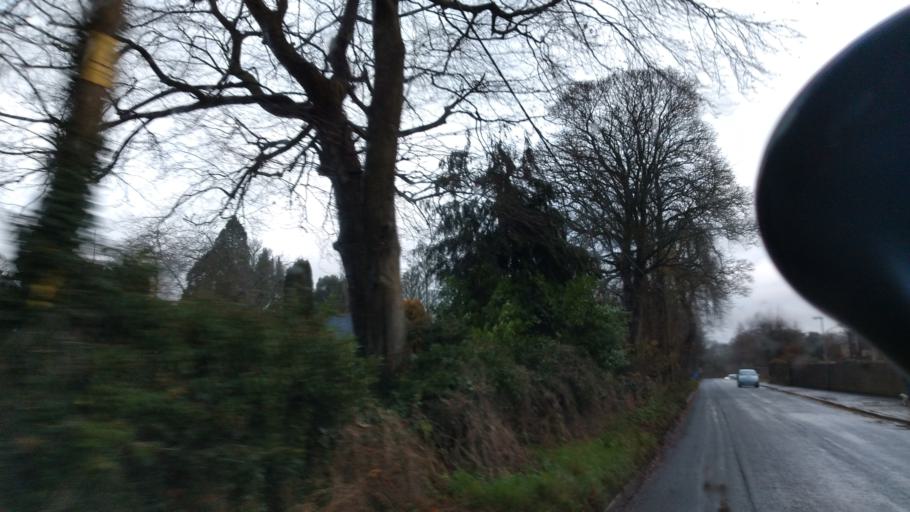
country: GB
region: England
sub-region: Wiltshire
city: Box
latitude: 51.4287
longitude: -2.2259
